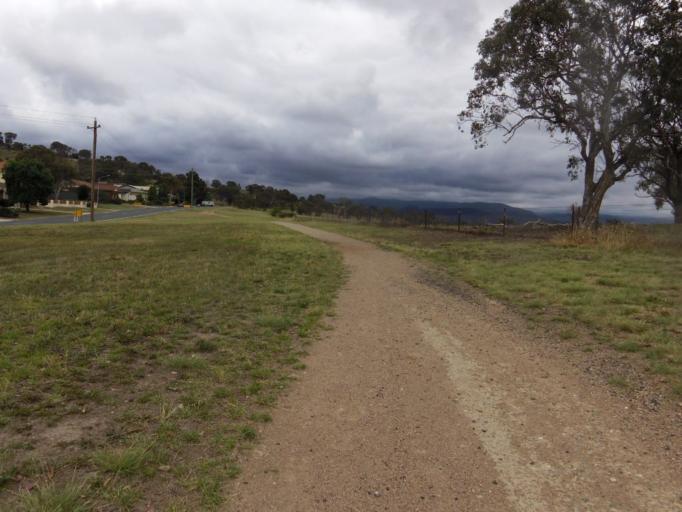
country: AU
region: Australian Capital Territory
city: Macquarie
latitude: -35.3465
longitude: 149.0271
